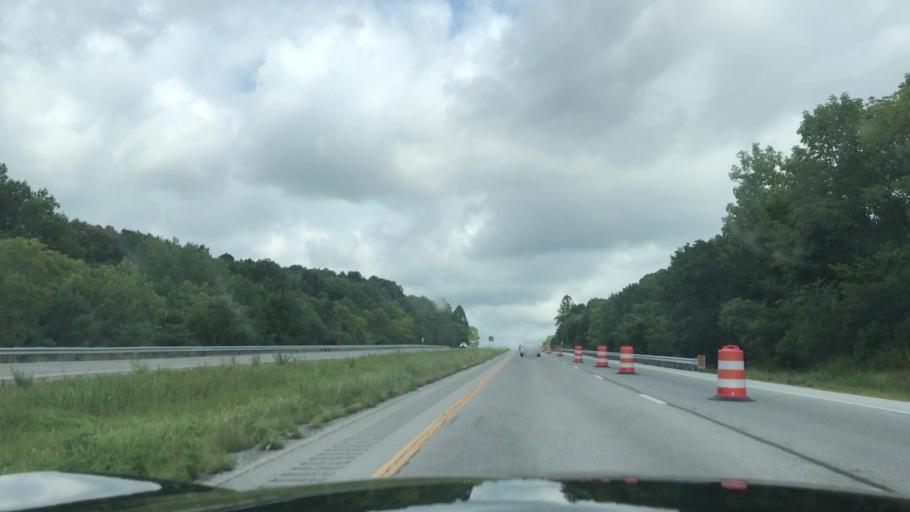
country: US
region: Kentucky
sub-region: Butler County
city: Morgantown
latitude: 37.0946
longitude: -86.6309
